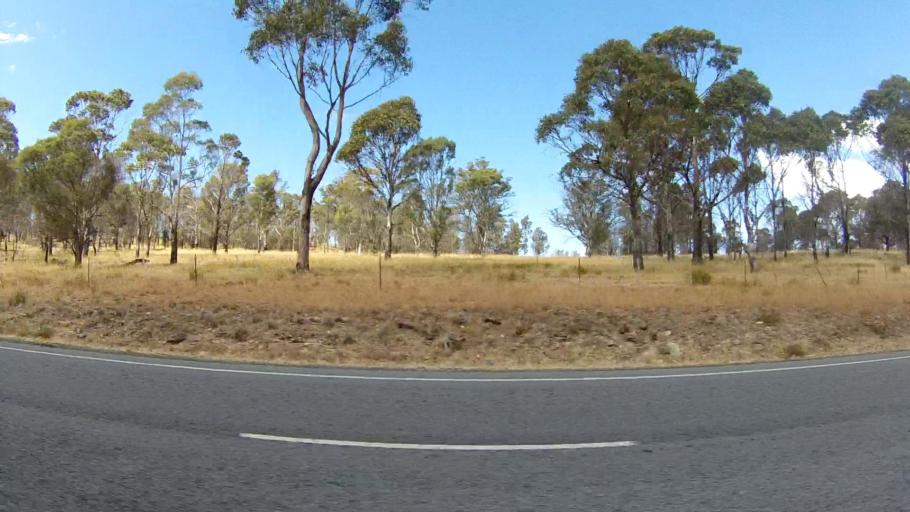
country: AU
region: Tasmania
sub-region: Sorell
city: Sorell
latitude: -42.6156
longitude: 147.6468
